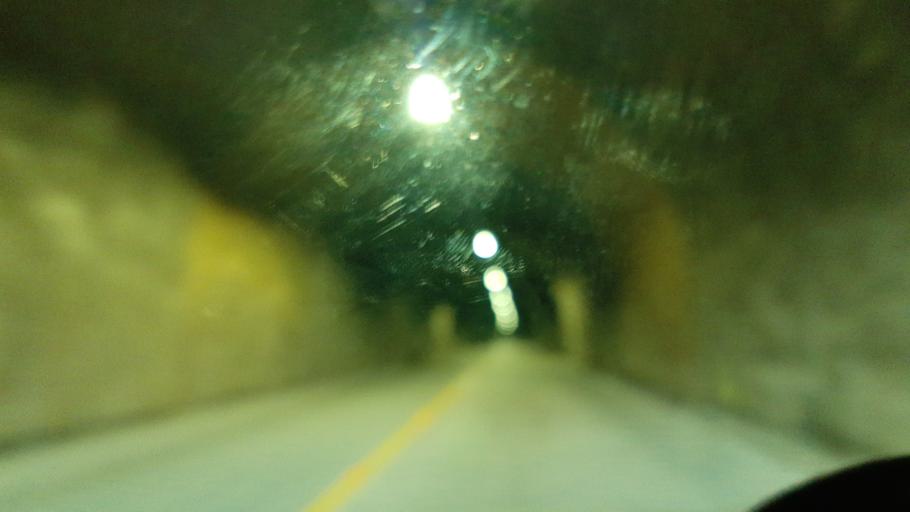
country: CO
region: Boyaca
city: Somondoco
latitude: 4.9972
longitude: -73.3523
